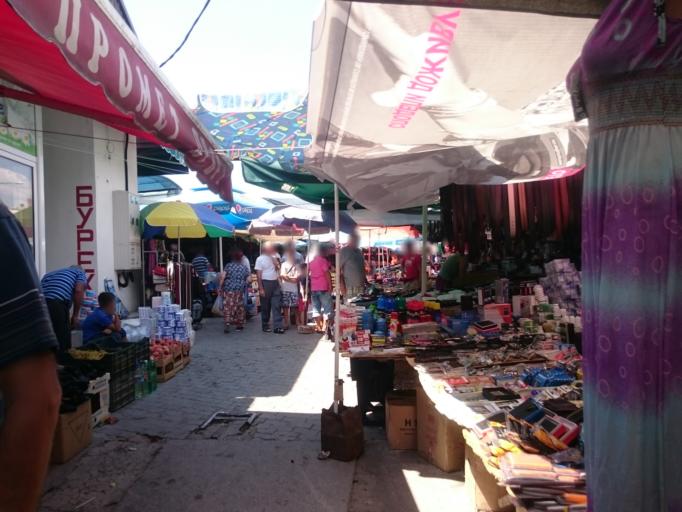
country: MK
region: Prilep
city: Prilep
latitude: 41.3445
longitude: 21.5554
